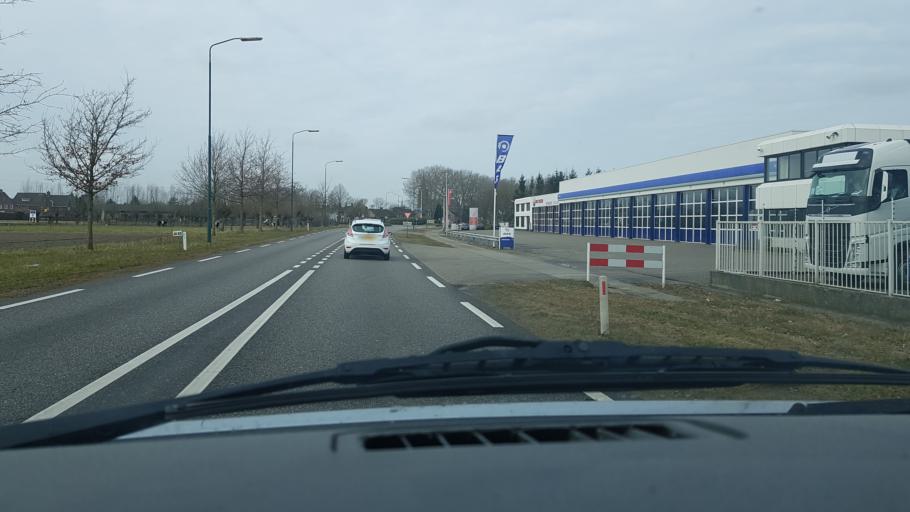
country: NL
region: North Brabant
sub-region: Gemeente Veghel
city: Eerde
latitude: 51.6034
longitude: 5.5058
